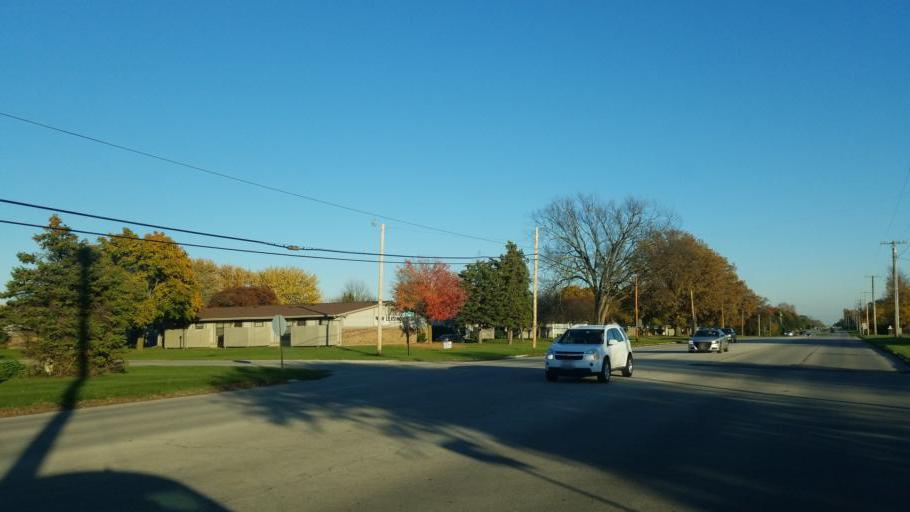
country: US
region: Ohio
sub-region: Sandusky County
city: Fremont
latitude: 41.3390
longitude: -83.0826
